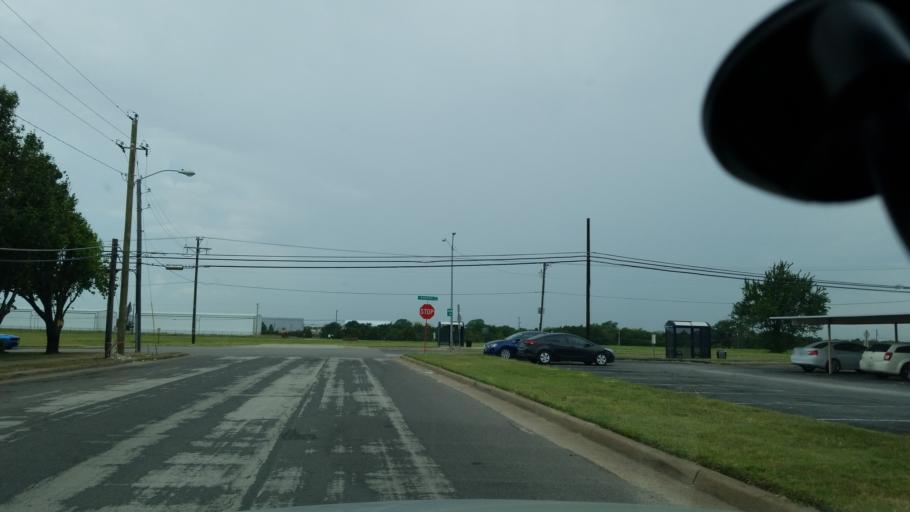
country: US
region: Texas
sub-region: Dallas County
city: Duncanville
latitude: 32.6828
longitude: -96.8564
